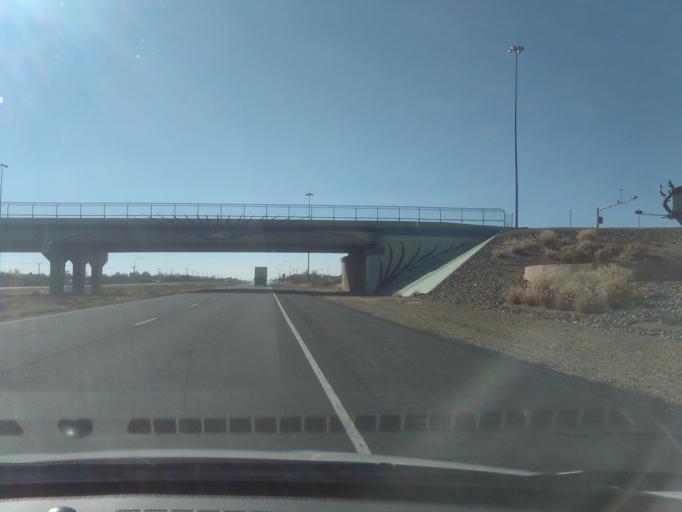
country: US
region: New Mexico
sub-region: Valencia County
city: Los Lunas
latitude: 34.8152
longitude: -106.7611
